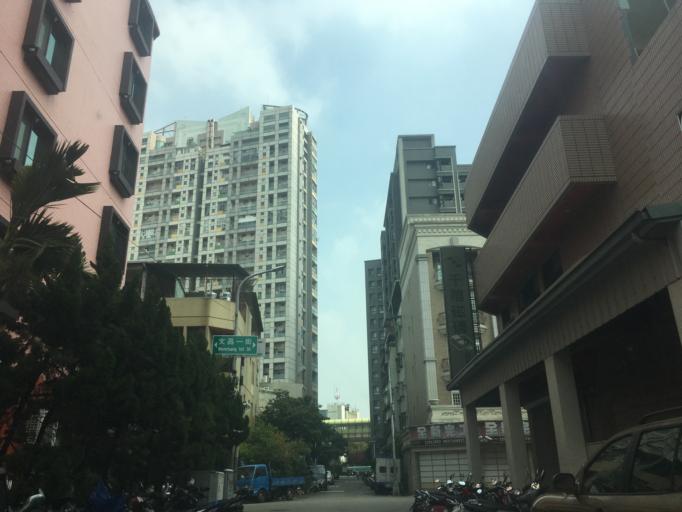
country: TW
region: Taiwan
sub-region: Taichung City
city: Taichung
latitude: 24.1721
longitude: 120.6751
